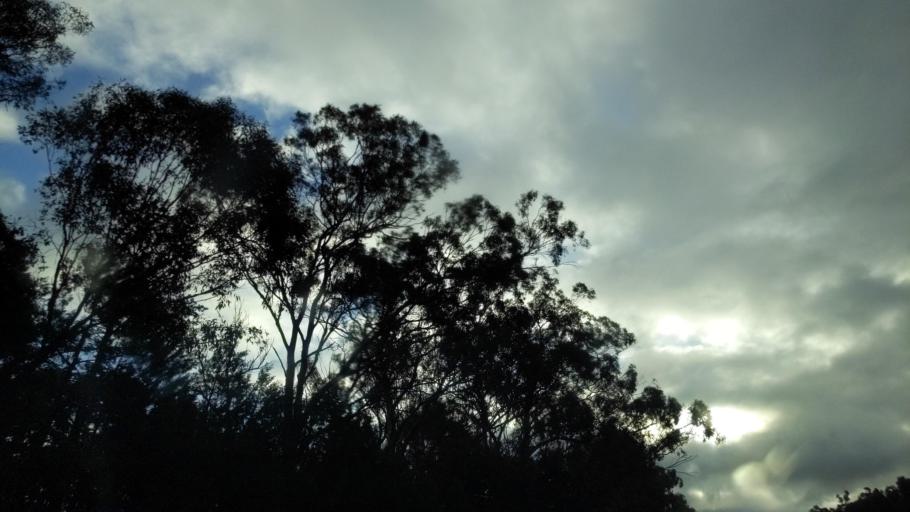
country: AU
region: New South Wales
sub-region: Coolamon
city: Coolamon
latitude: -34.8628
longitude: 147.2395
